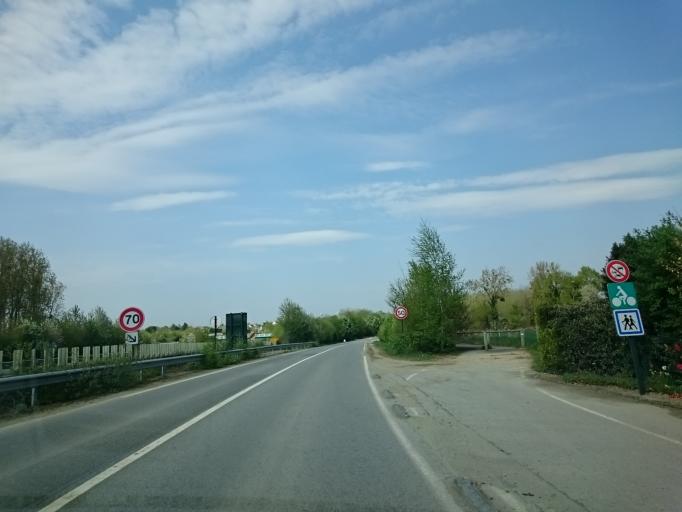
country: FR
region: Brittany
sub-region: Departement d'Ille-et-Vilaine
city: Vern-sur-Seiche
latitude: 48.0330
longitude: -1.6000
